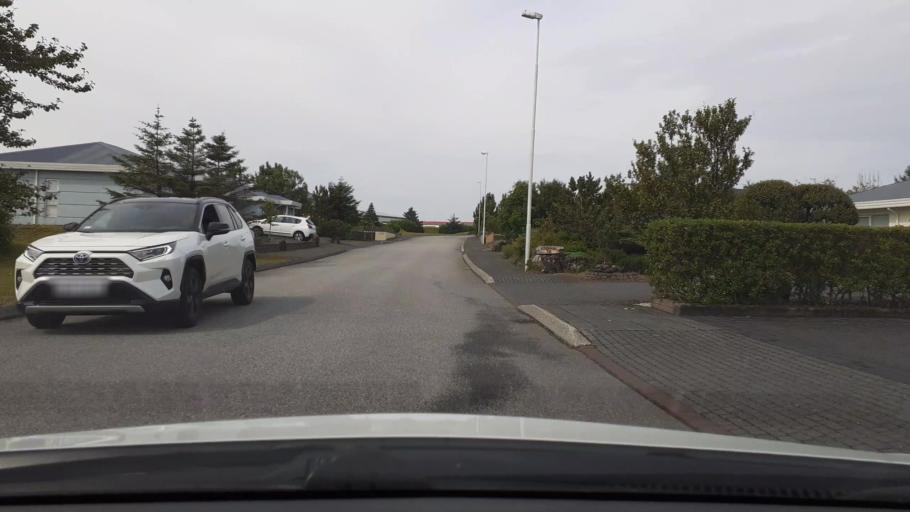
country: IS
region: Southern Peninsula
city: Reykjanesbaer
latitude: 63.9967
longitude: -22.5722
